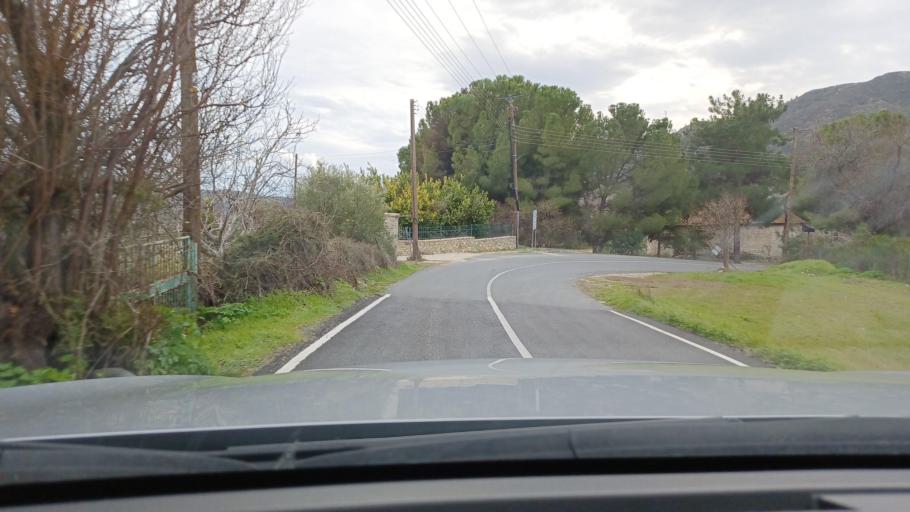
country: CY
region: Limassol
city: Pelendri
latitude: 34.8251
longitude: 32.8967
